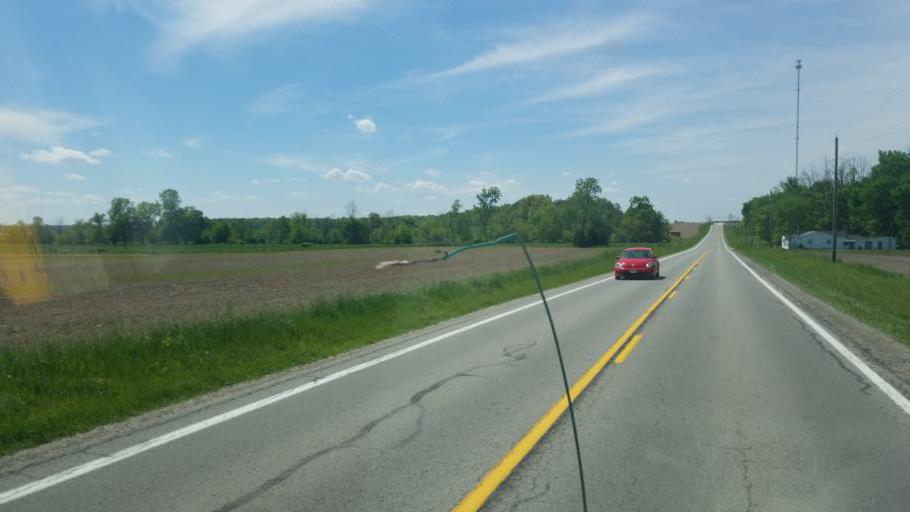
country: US
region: Ohio
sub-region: Huron County
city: Willard
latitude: 41.0727
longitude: -82.9079
